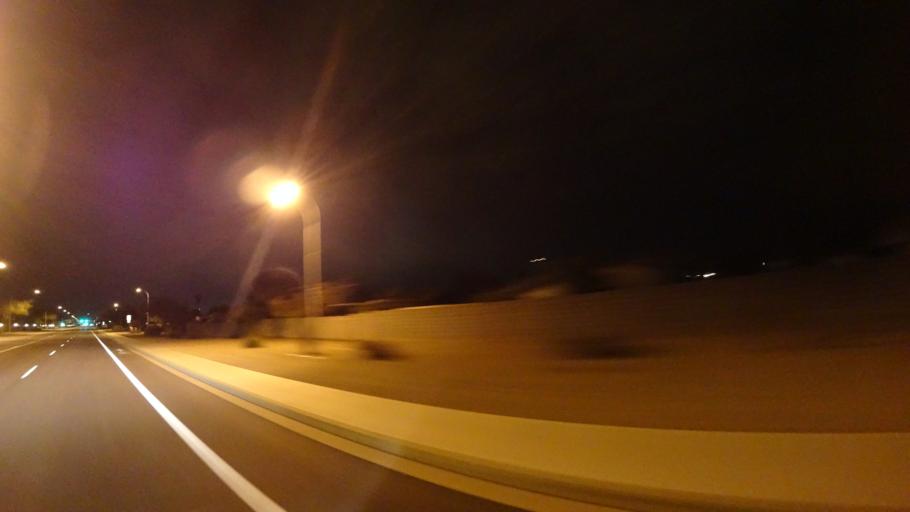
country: US
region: Arizona
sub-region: Pinal County
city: Apache Junction
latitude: 33.3793
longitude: -111.6564
